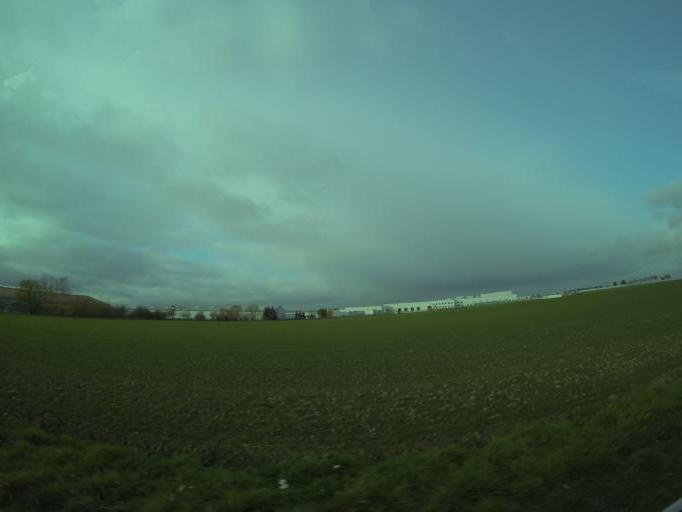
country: DE
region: Thuringia
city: Schmolln
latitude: 50.8894
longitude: 12.3908
